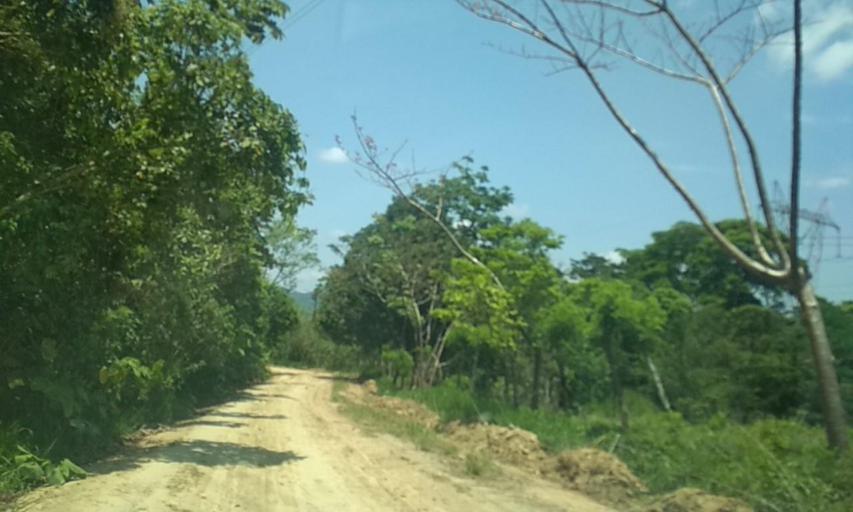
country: MX
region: Chiapas
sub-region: Tecpatan
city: Raudales Malpaso
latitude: 17.3953
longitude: -93.7235
